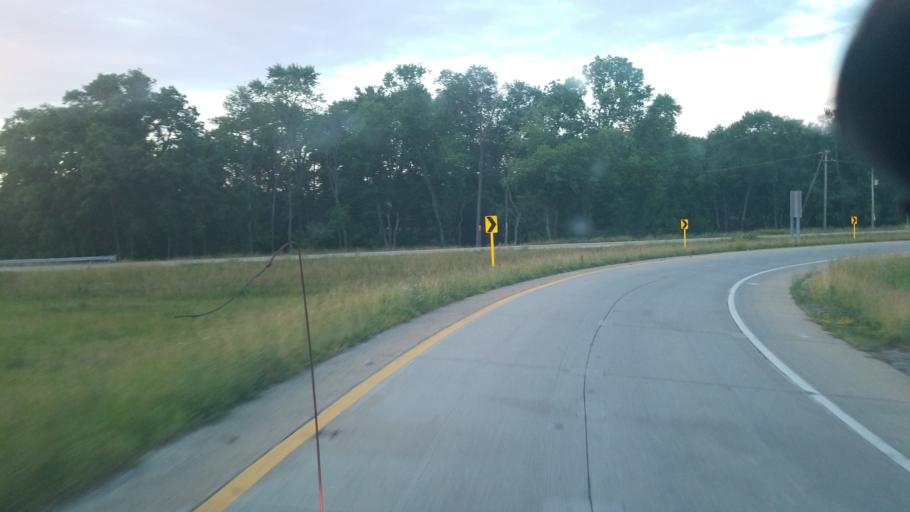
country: US
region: Ohio
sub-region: Licking County
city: Buckeye Lake
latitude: 39.9465
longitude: -82.4803
